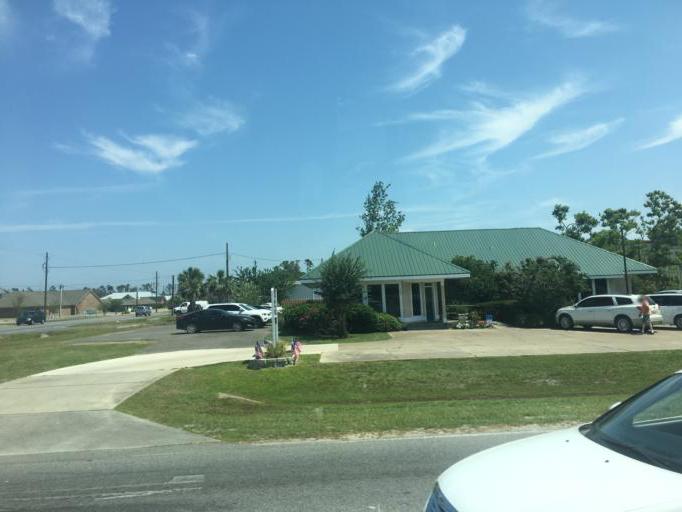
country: US
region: Florida
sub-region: Bay County
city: Lynn Haven
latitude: 30.2187
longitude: -85.6617
